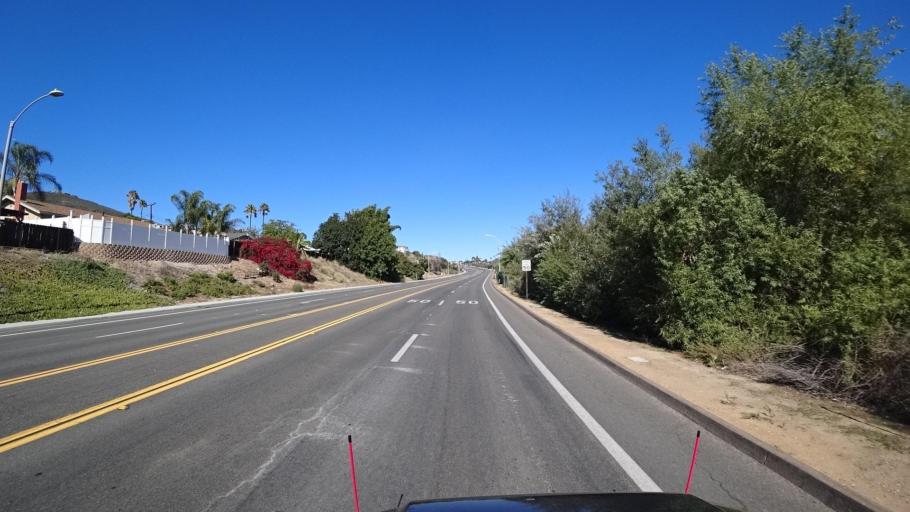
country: US
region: California
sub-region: San Diego County
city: La Presa
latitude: 32.7183
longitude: -116.9747
